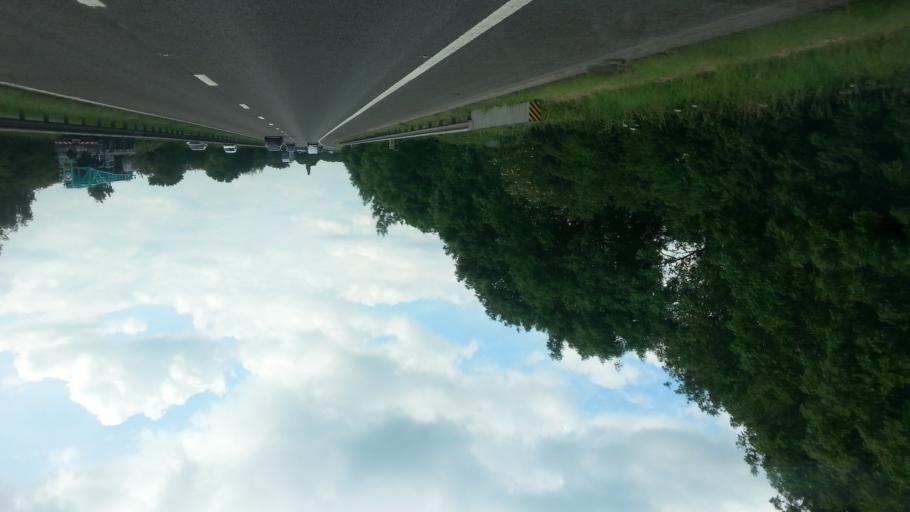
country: GB
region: England
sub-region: Doncaster
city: Tickhill
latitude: 53.4276
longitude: -1.0937
